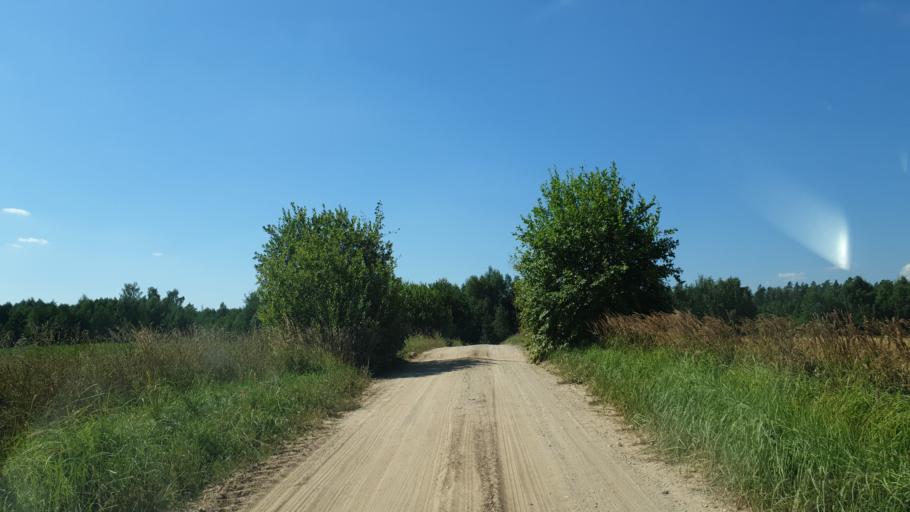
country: LT
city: Sirvintos
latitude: 54.9003
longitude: 24.9049
